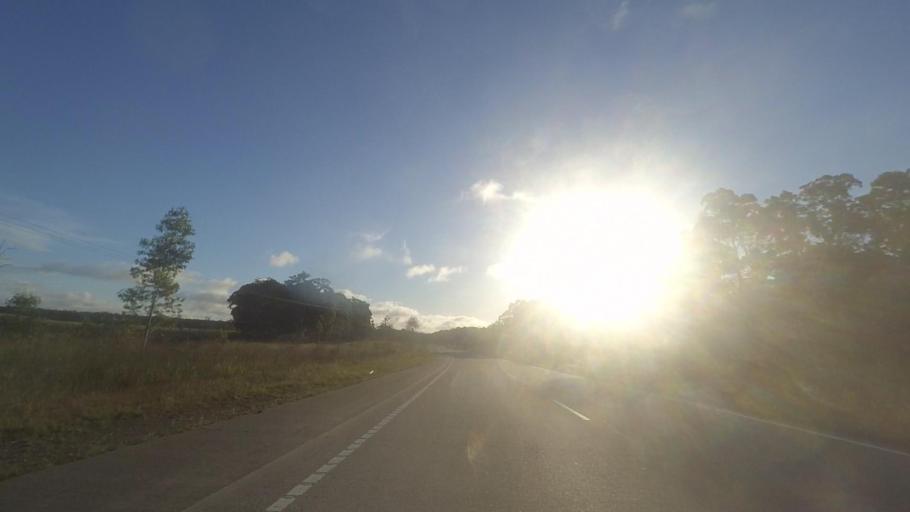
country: AU
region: New South Wales
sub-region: Great Lakes
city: Hawks Nest
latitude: -32.5383
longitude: 152.1705
